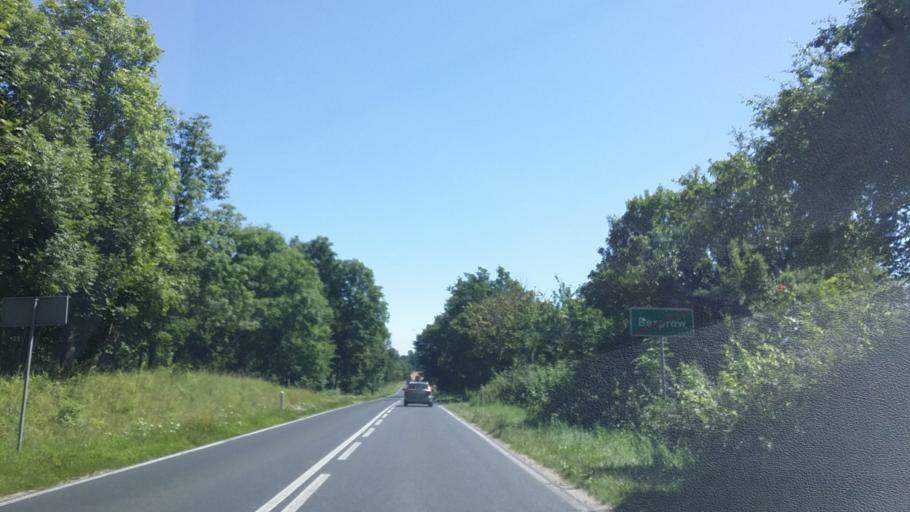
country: PL
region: West Pomeranian Voivodeship
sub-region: Powiat kolobrzeski
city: Kolobrzeg
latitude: 54.1286
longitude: 15.5685
